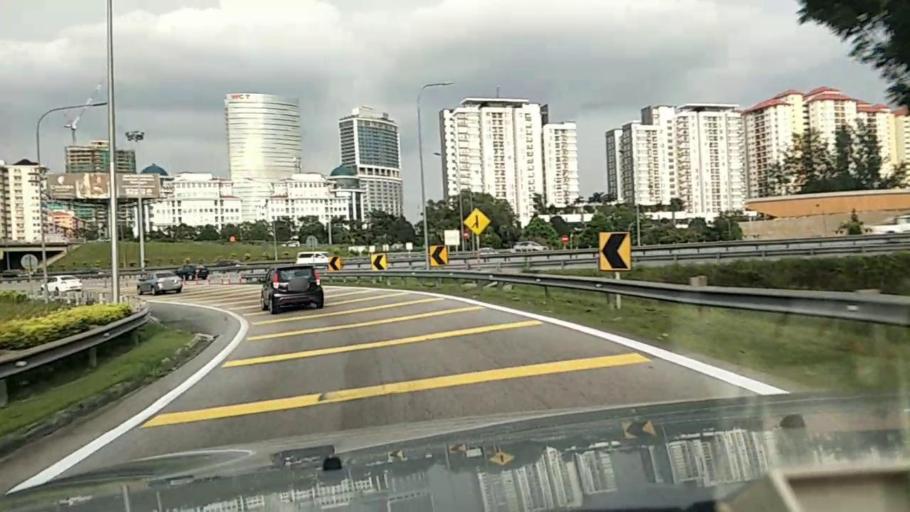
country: MY
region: Selangor
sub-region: Petaling
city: Petaling Jaya
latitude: 3.1058
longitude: 101.5889
